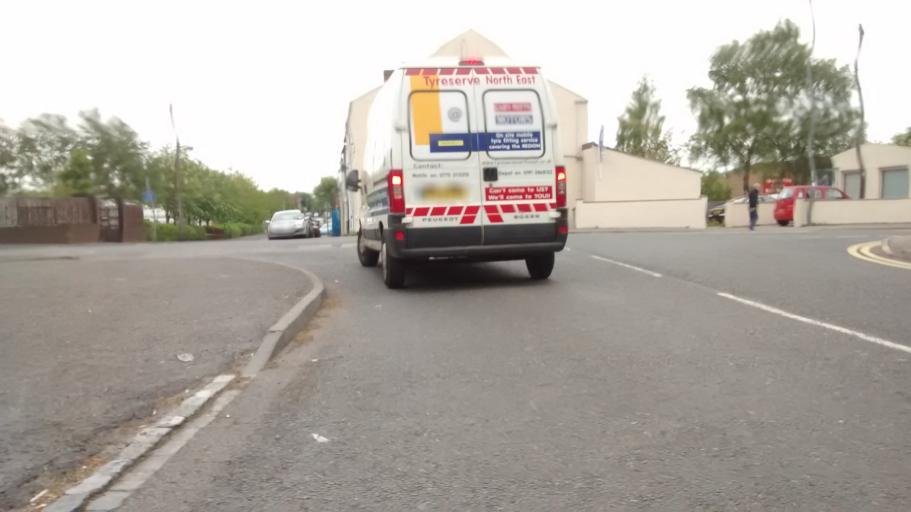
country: GB
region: England
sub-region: County Durham
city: Durham
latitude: 54.7795
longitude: -1.5395
